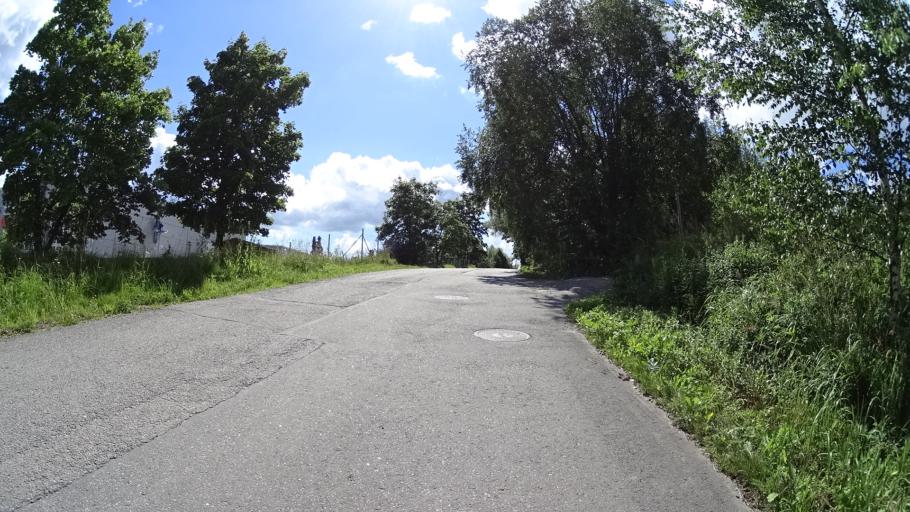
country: FI
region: Uusimaa
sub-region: Helsinki
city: Teekkarikylae
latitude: 60.2973
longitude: 24.8794
